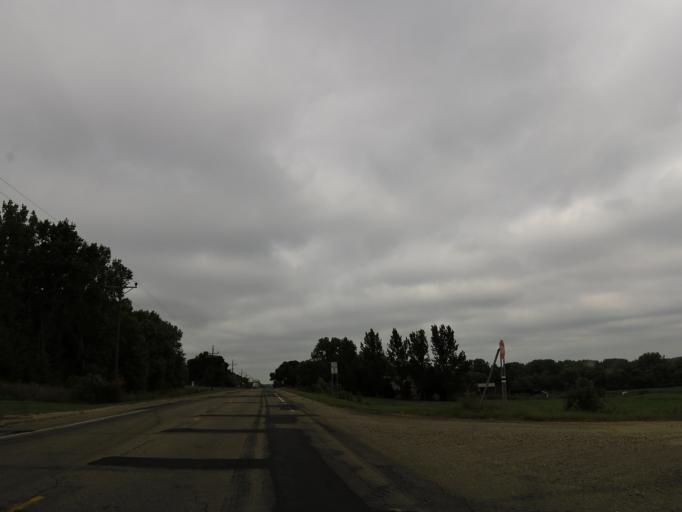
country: US
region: Minnesota
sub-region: Yellow Medicine County
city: Granite Falls
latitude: 44.8441
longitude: -95.6157
